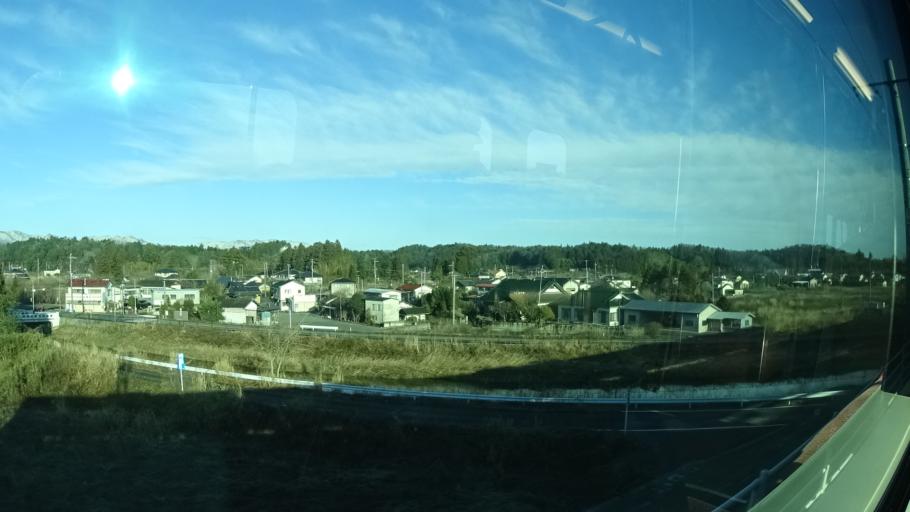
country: JP
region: Fukushima
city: Namie
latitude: 37.4392
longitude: 141.0013
